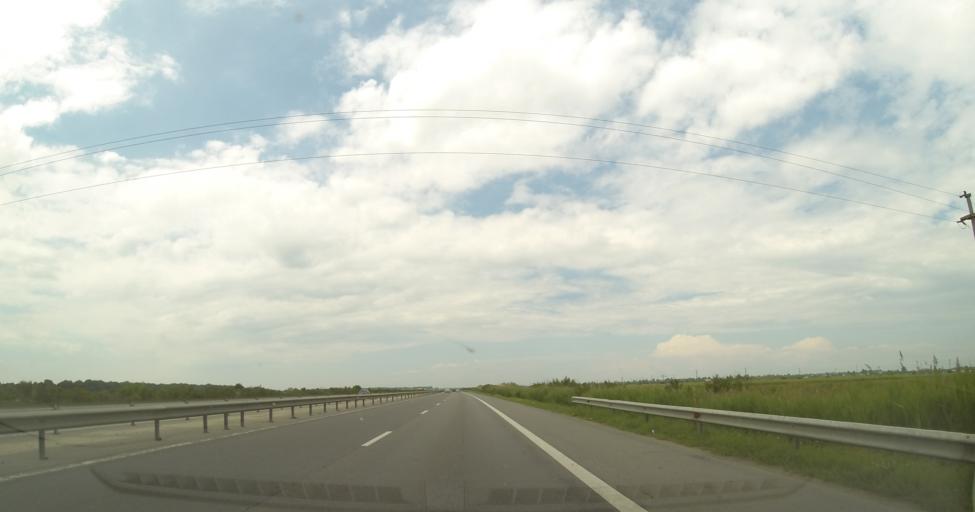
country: RO
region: Dambovita
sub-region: Comuna Corbii Mari
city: Corbii Mari
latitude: 44.5635
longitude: 25.4926
